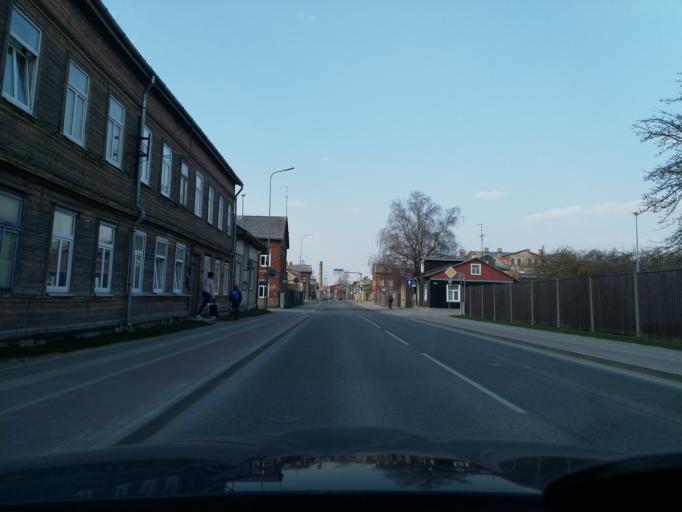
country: LV
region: Liepaja
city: Liepaja
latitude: 56.5046
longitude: 21.0240
